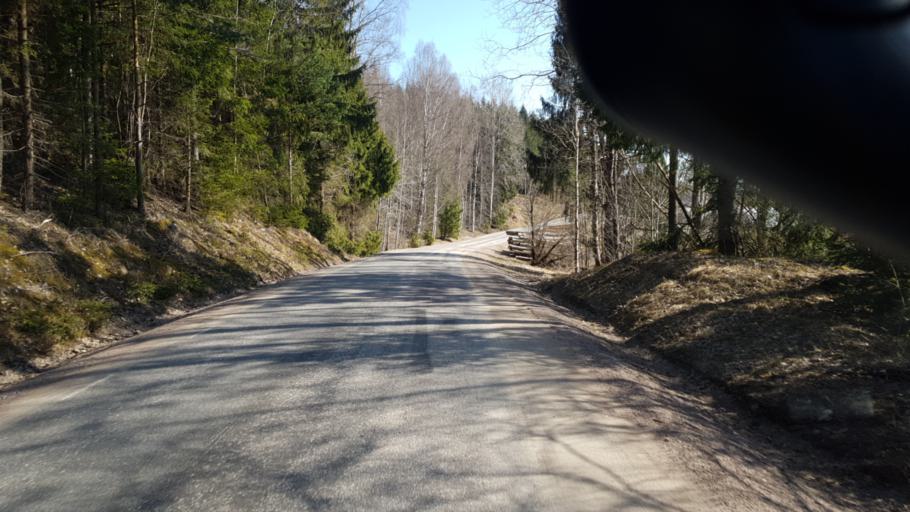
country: SE
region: Vaermland
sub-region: Arvika Kommun
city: Arvika
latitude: 59.6613
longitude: 12.7978
